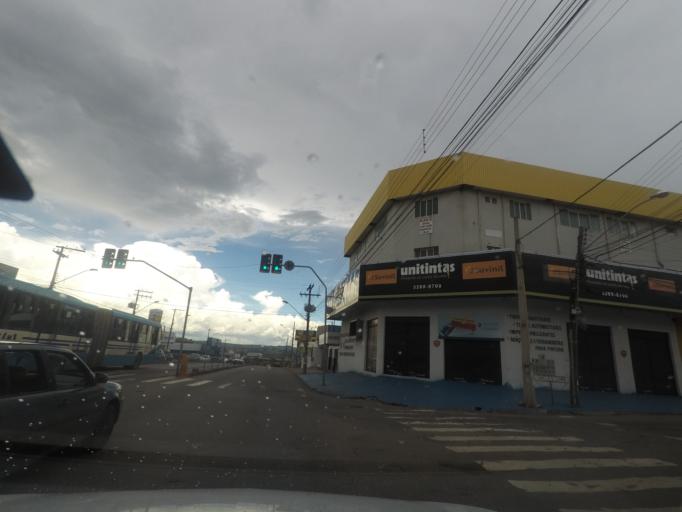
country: BR
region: Goias
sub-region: Goiania
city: Goiania
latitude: -16.6707
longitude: -49.2301
